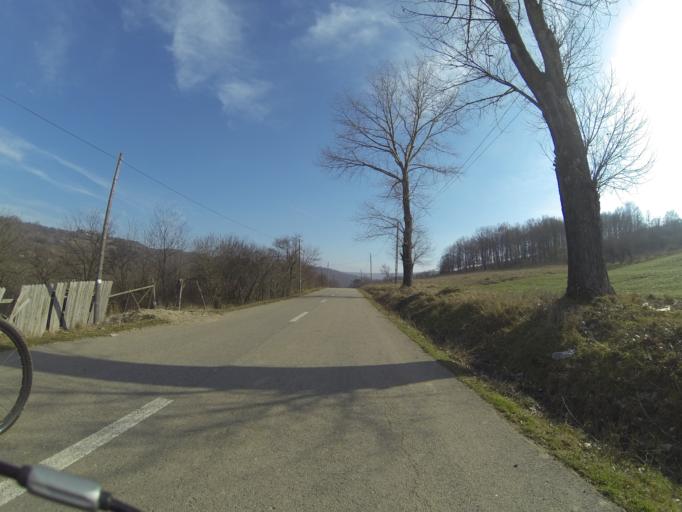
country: RO
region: Mehedinti
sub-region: Comuna Poroina Mare
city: Poroina Mare
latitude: 44.4934
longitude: 22.9307
